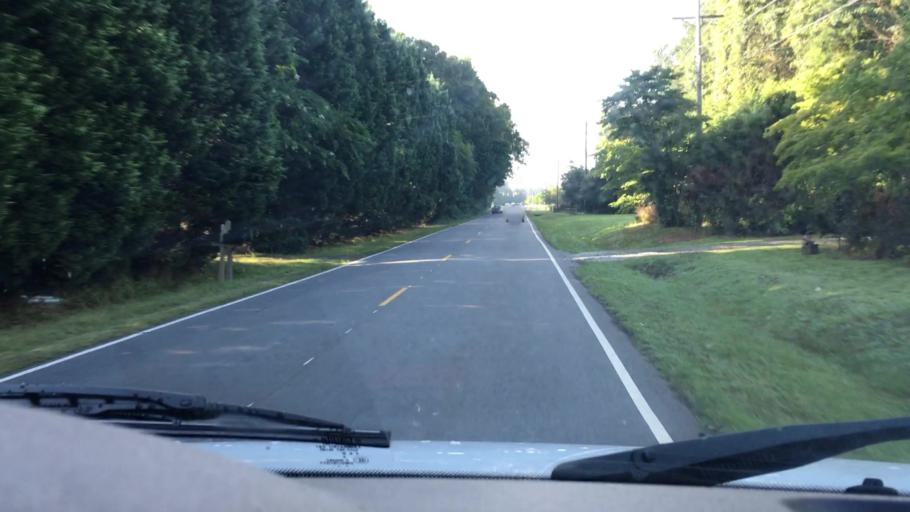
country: US
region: North Carolina
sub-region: Mecklenburg County
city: Huntersville
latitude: 35.4050
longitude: -80.9255
